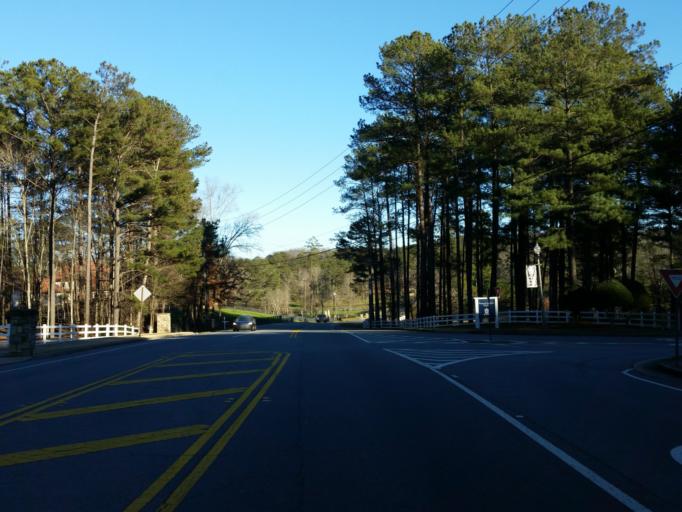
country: US
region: Georgia
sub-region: Cobb County
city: Kennesaw
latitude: 33.9767
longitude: -84.6884
